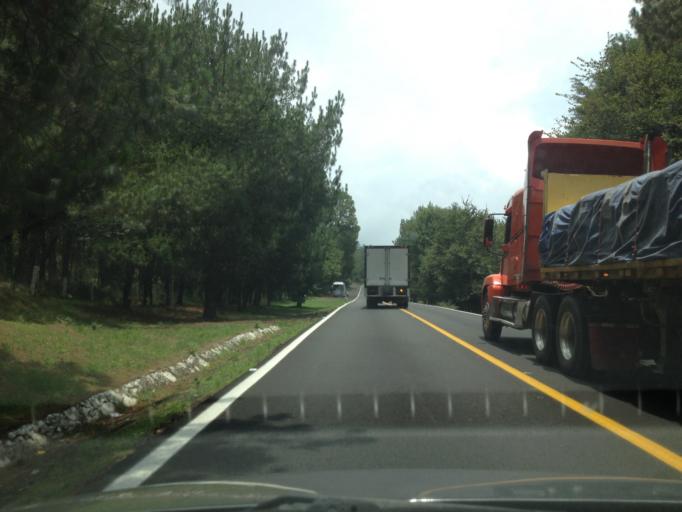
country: MX
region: Michoacan
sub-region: Patzcuaro
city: Santa Maria Huiramangaro (San Juan Tumbio)
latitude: 19.4976
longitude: -101.7691
